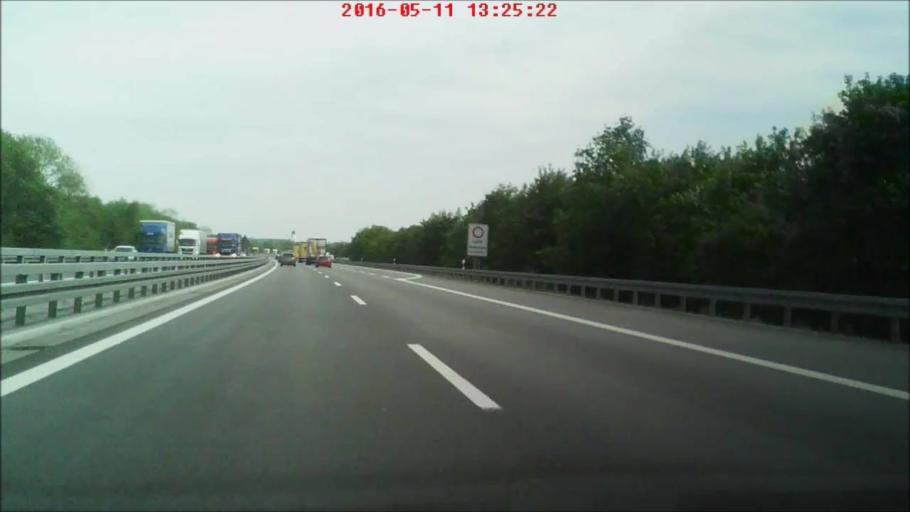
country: AT
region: Upper Austria
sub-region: Politischer Bezirk Scharding
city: Sankt Florian am Inn
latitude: 48.4178
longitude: 13.4059
